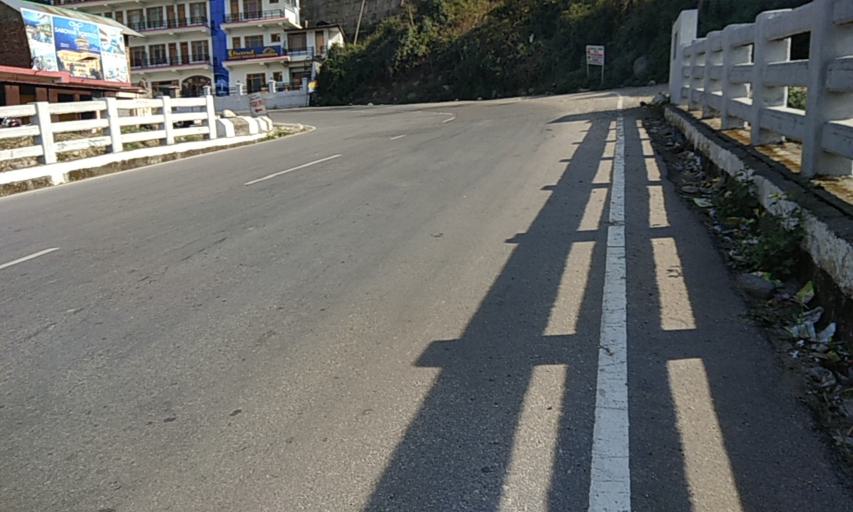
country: IN
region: Himachal Pradesh
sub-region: Kangra
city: Dharmsala
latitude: 32.1477
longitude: 76.4216
